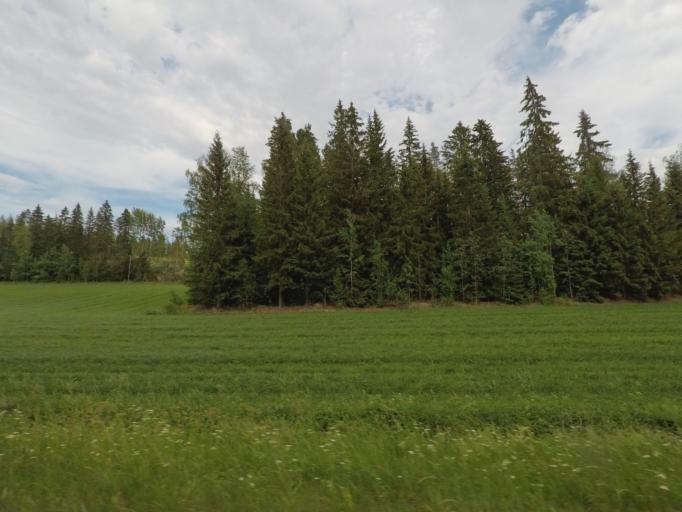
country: FI
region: Paijanne Tavastia
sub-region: Lahti
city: Hollola
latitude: 60.8661
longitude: 25.5014
